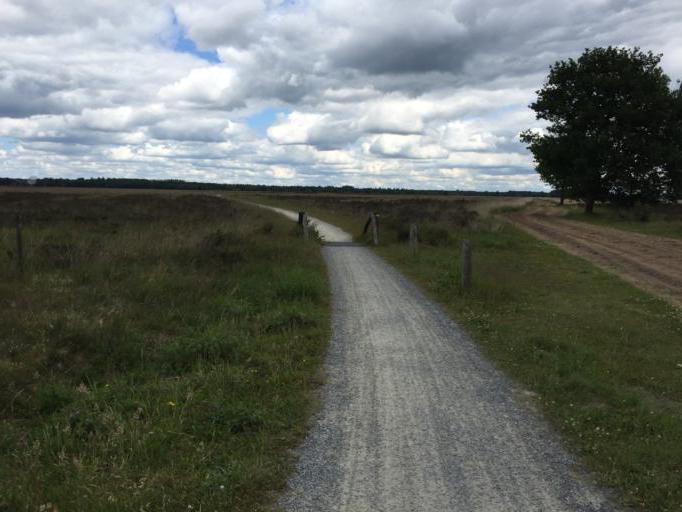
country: NL
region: Drenthe
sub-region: Gemeente Westerveld
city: Dwingeloo
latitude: 52.7965
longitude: 6.3963
